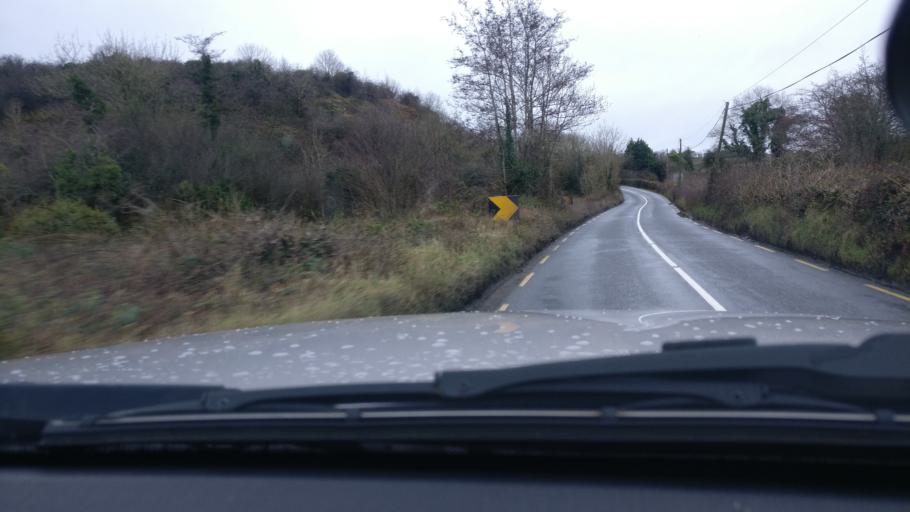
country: IE
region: Leinster
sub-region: An Longfort
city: Granard
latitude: 53.8041
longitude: -7.3800
